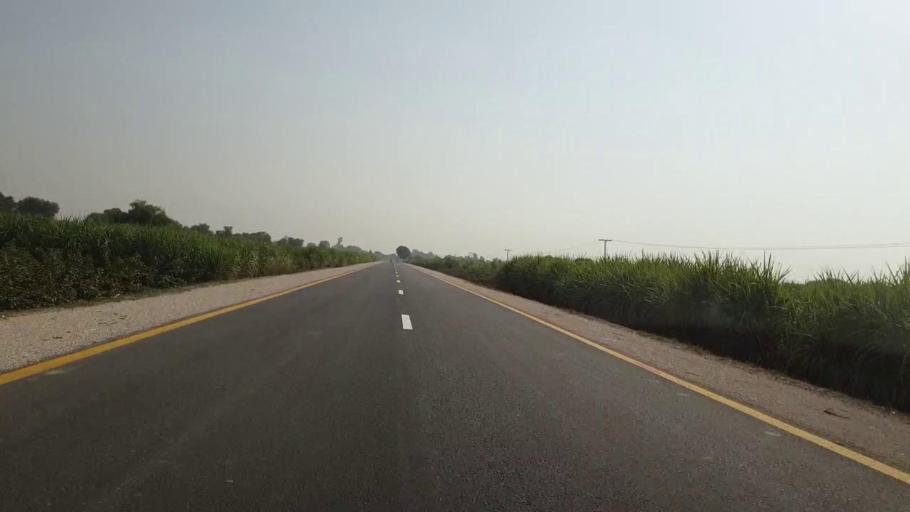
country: PK
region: Sindh
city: Bhan
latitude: 26.6094
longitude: 67.7788
